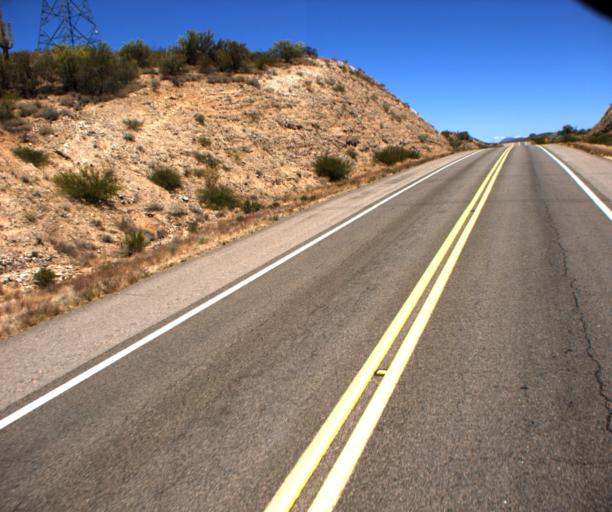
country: US
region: Arizona
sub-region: Yavapai County
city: Bagdad
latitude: 34.4293
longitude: -113.2453
